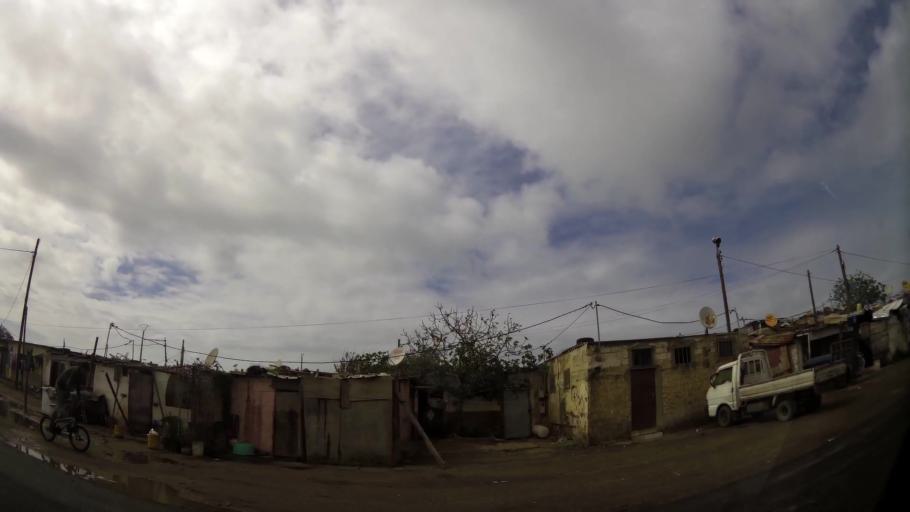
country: MA
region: Grand Casablanca
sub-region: Mohammedia
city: Mohammedia
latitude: 33.6516
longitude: -7.4629
